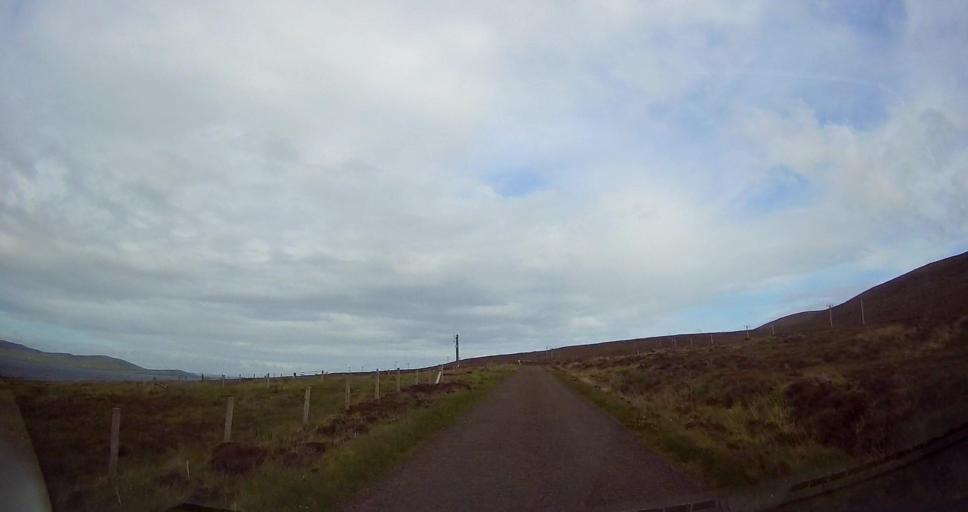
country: GB
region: Scotland
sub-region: Orkney Islands
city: Stromness
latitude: 58.9021
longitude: -3.2950
